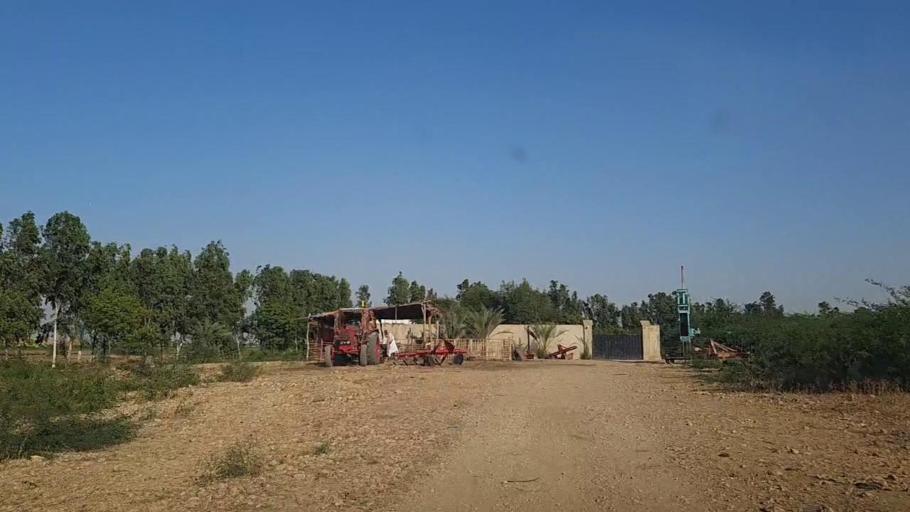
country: PK
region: Sindh
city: Daro Mehar
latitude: 25.0500
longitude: 68.1429
